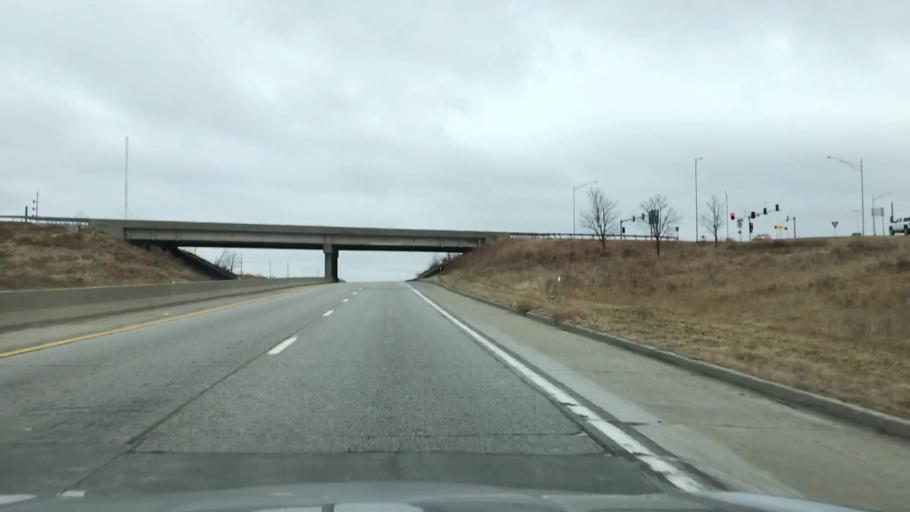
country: US
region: Missouri
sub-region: Jackson County
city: East Independence
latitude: 39.1160
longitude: -94.3844
